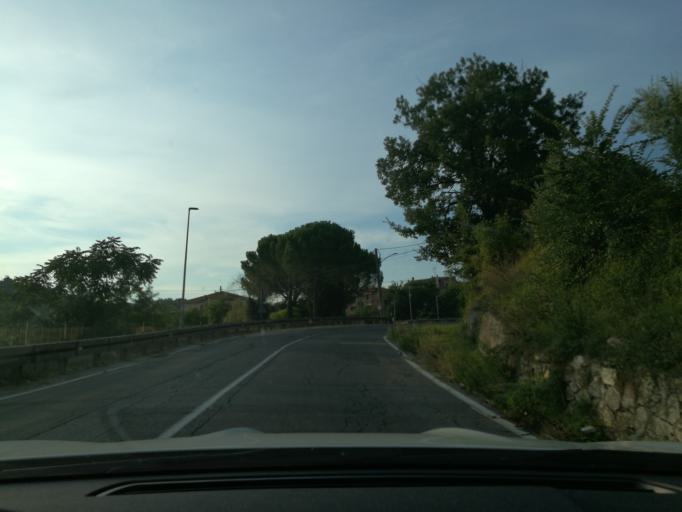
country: IT
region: Umbria
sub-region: Provincia di Terni
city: San Gemini
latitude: 42.6234
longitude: 12.5488
